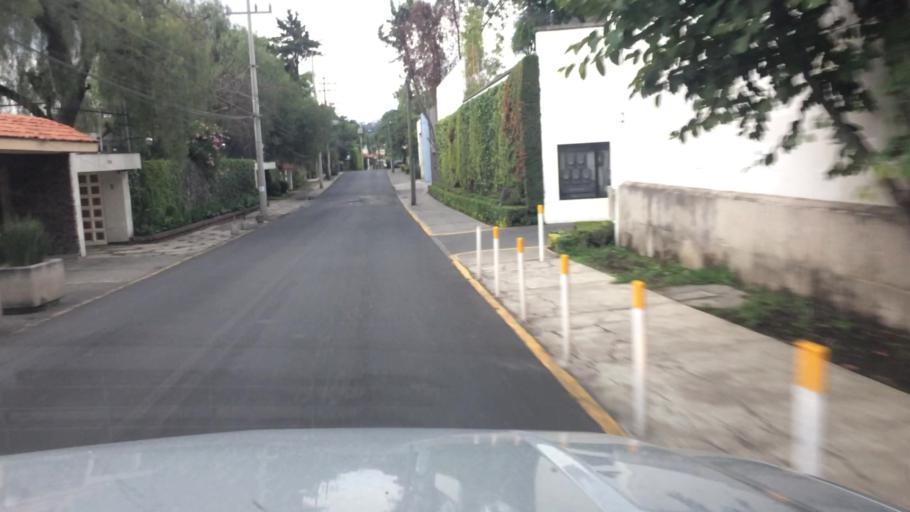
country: MX
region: Mexico City
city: Magdalena Contreras
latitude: 19.3171
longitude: -99.2093
